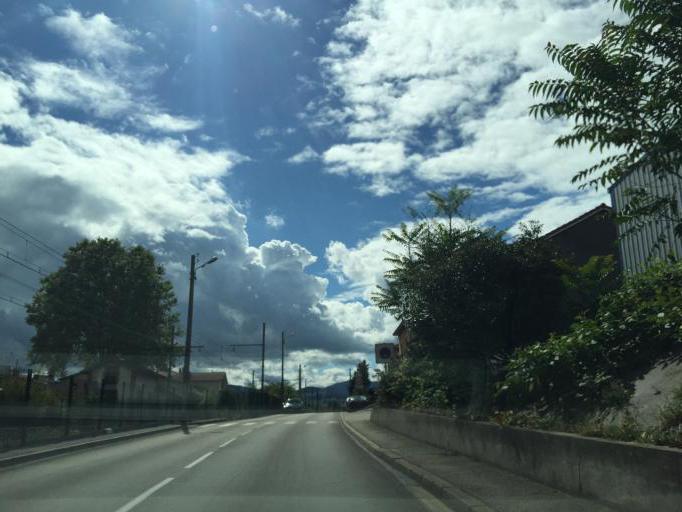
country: FR
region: Rhone-Alpes
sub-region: Departement de la Loire
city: Lorette
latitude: 45.5064
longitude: 4.5701
